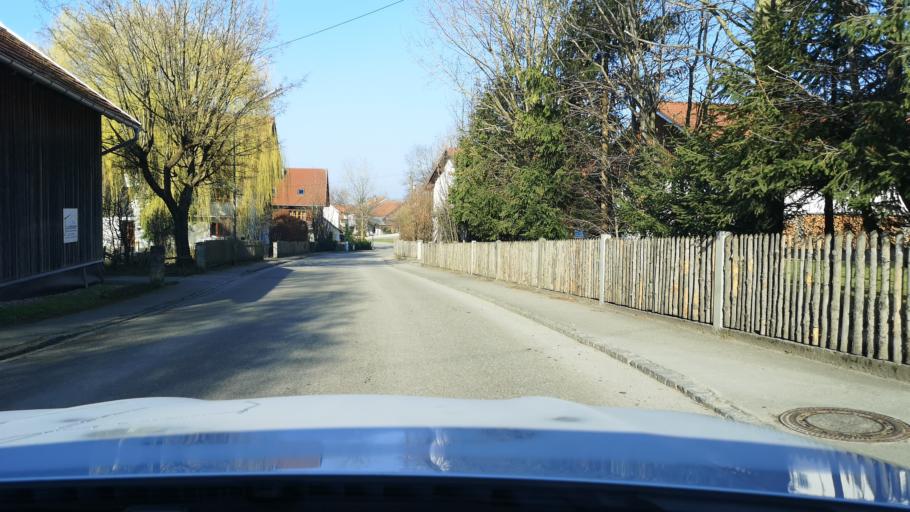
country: DE
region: Bavaria
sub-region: Upper Bavaria
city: Finsing
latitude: 48.2157
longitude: 11.8290
